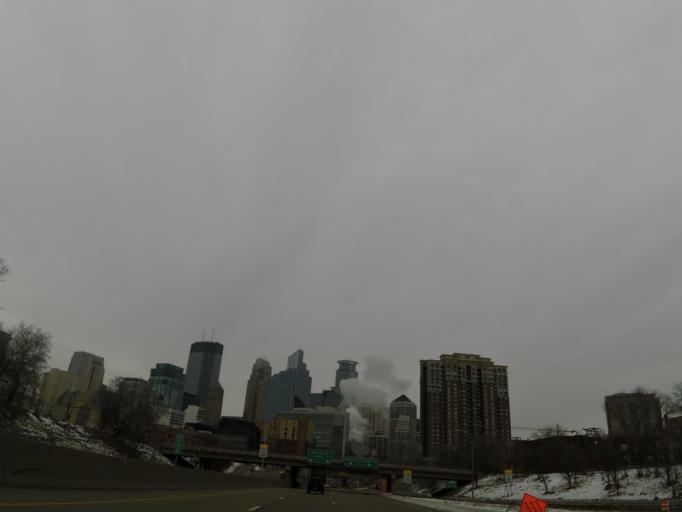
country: US
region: Minnesota
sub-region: Hennepin County
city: Minneapolis
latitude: 44.9669
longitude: -93.2698
